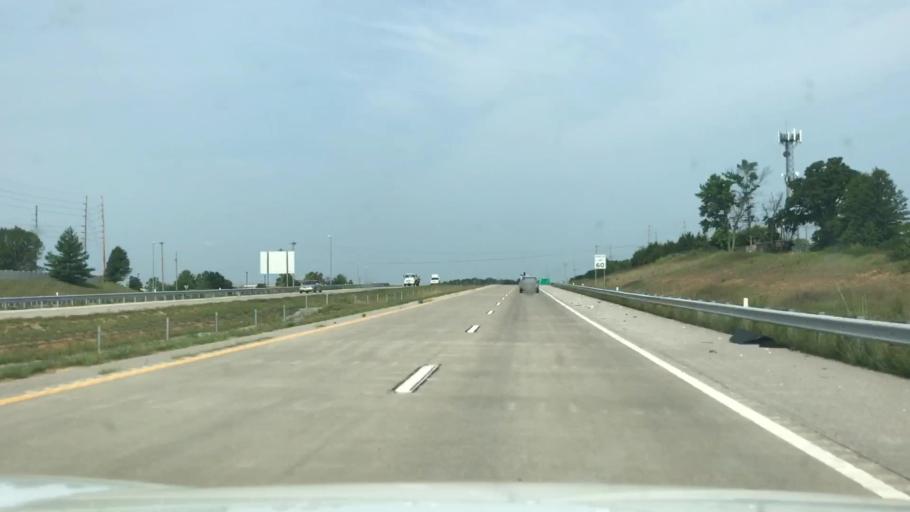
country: US
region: Missouri
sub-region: Saint Charles County
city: Dardenne Prairie
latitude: 38.7577
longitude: -90.7106
